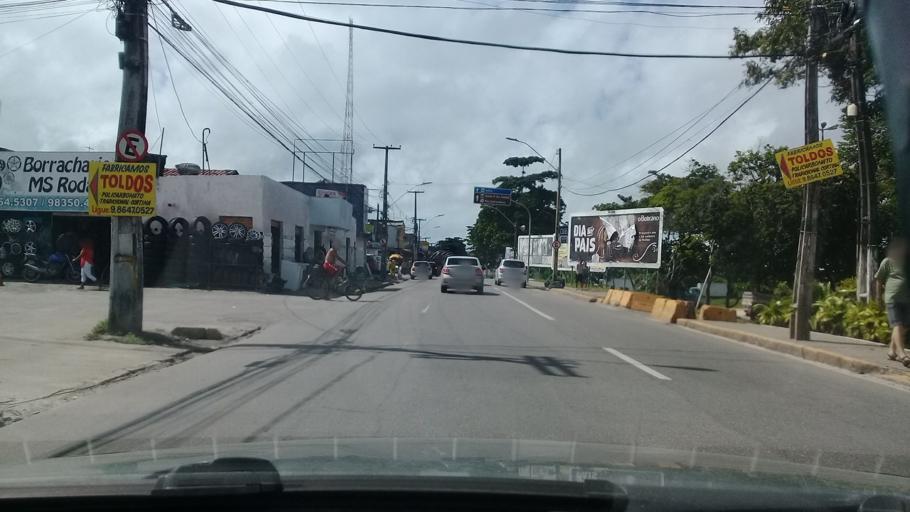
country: BR
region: Pernambuco
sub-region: Jaboatao Dos Guararapes
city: Jaboatao
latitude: -8.1640
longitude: -34.9223
